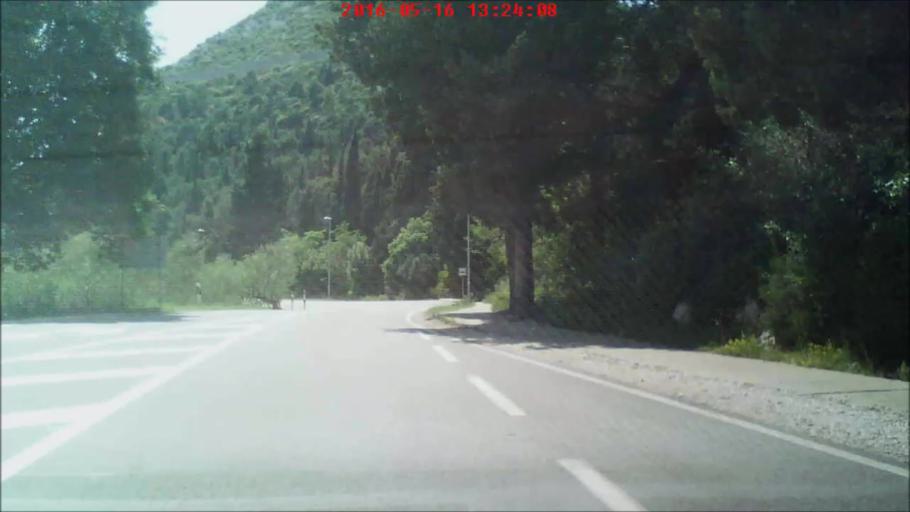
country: HR
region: Dubrovacko-Neretvanska
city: Ston
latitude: 42.8452
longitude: 17.7060
